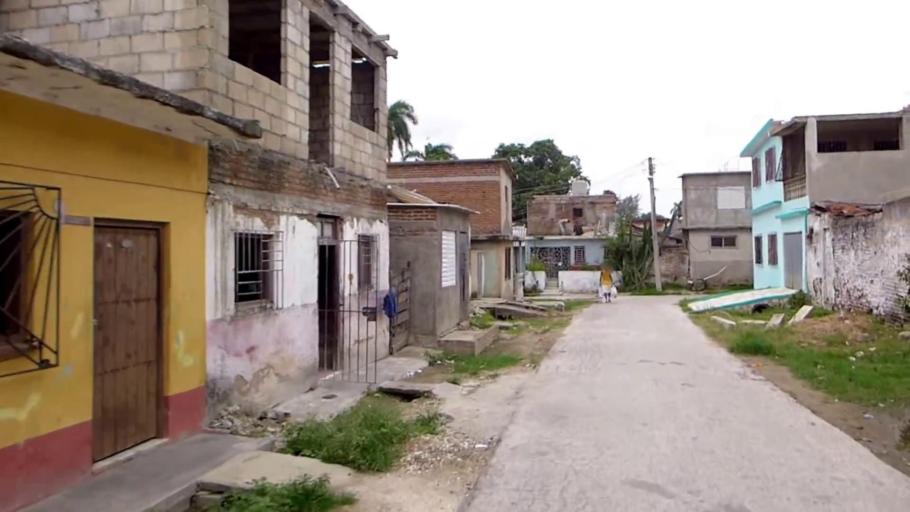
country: CU
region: Camaguey
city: Camaguey
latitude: 21.3793
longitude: -77.9135
